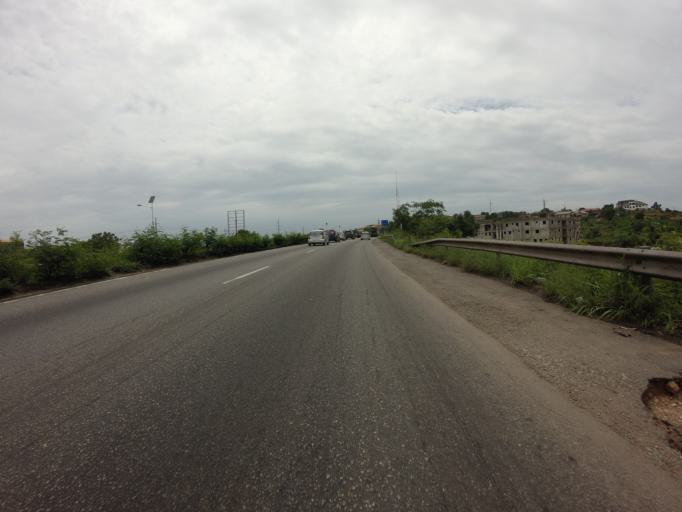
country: GH
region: Greater Accra
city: Dome
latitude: 5.6644
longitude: -0.2708
